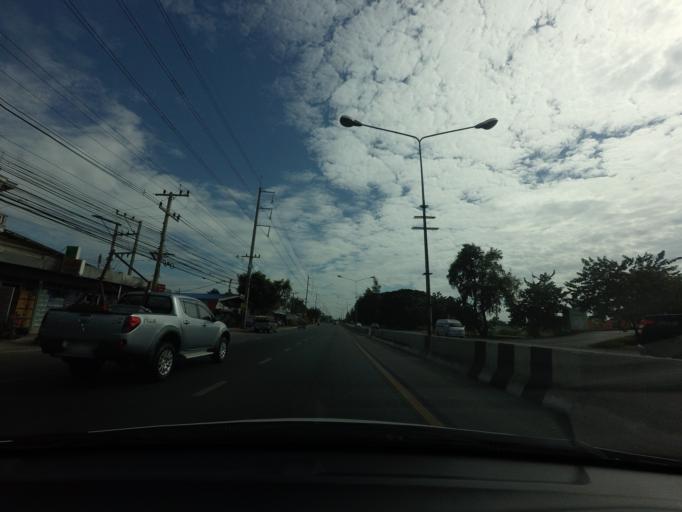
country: TH
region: Pathum Thani
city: Ban Rangsit
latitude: 14.0416
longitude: 100.7917
